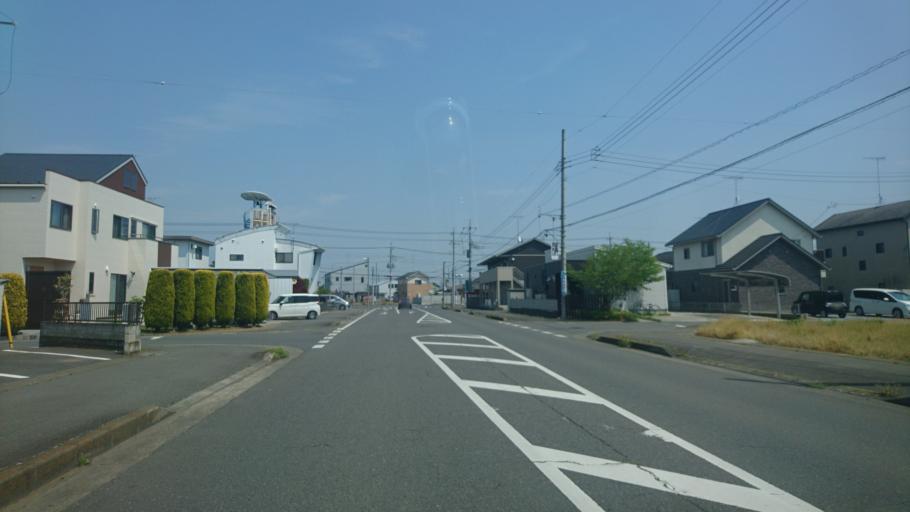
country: JP
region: Ibaraki
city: Yuki
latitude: 36.2907
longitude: 139.8797
